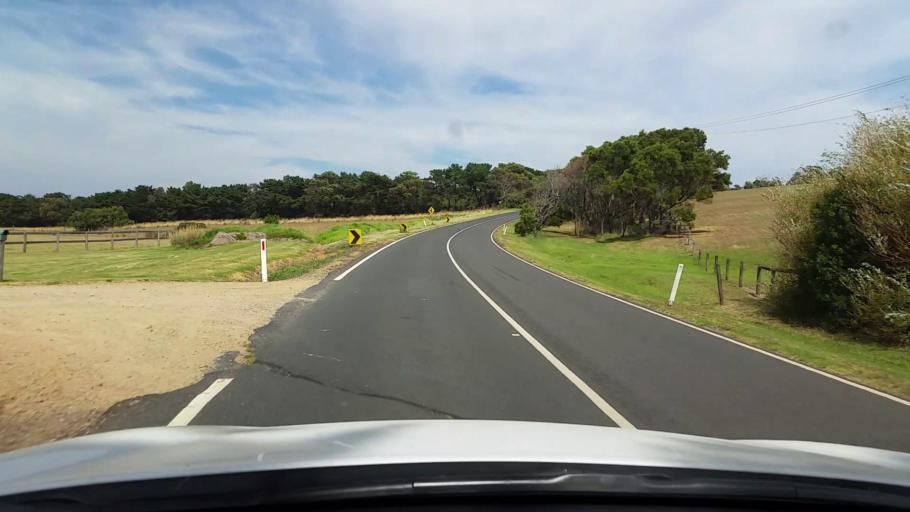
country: AU
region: Victoria
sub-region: Mornington Peninsula
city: Merricks
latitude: -38.4790
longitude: 144.9917
